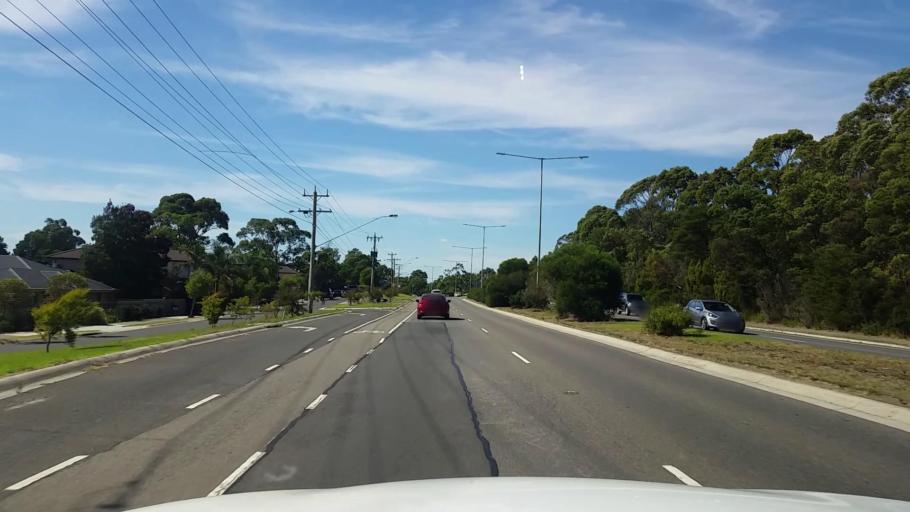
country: AU
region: Victoria
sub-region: Frankston
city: Langwarrin
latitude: -38.1555
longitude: 145.1783
